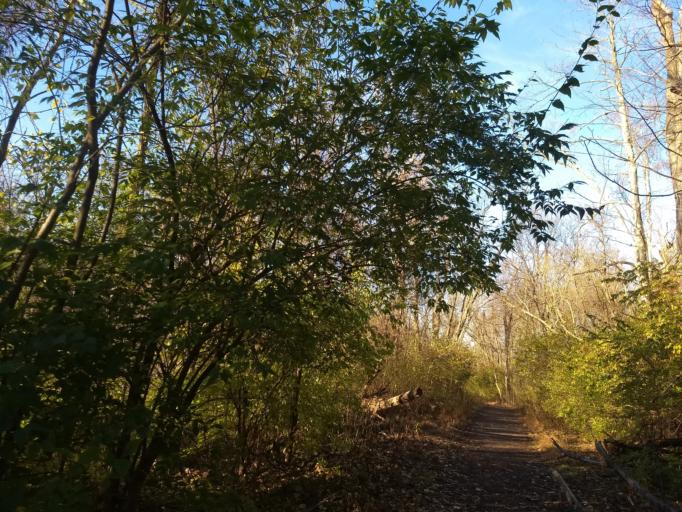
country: US
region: Pennsylvania
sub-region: Allegheny County
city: South Park Township
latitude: 40.3000
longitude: -80.0018
